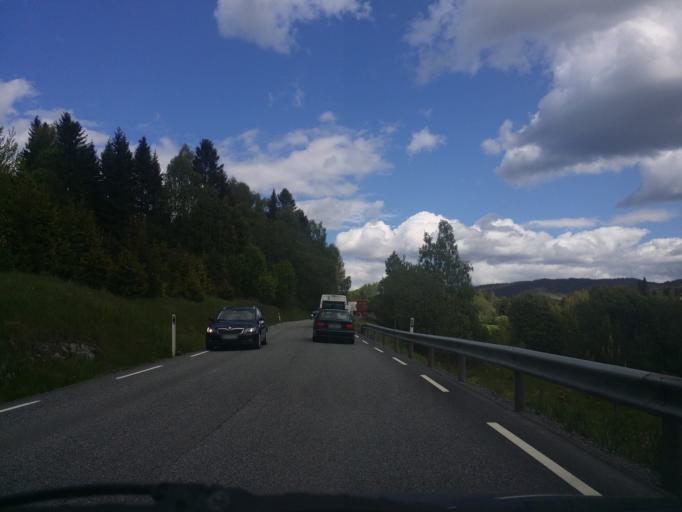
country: NO
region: Oppland
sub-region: Jevnaker
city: Jevnaker
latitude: 60.2674
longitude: 10.4726
